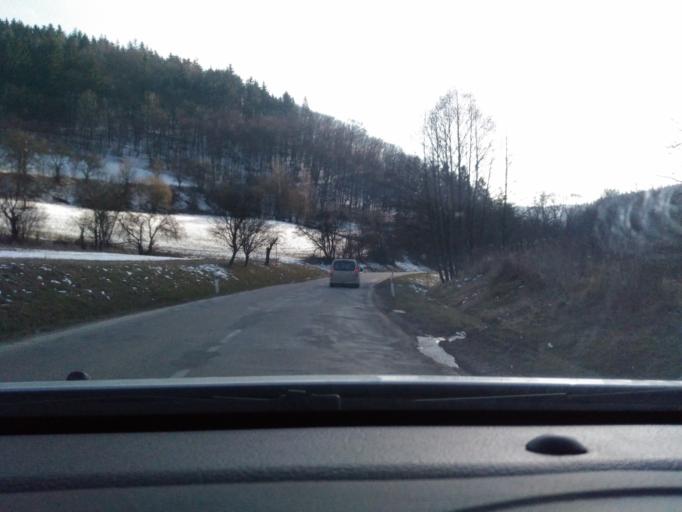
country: CZ
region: South Moravian
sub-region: Okres Brno-Venkov
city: Nedvedice
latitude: 49.4640
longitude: 16.3374
